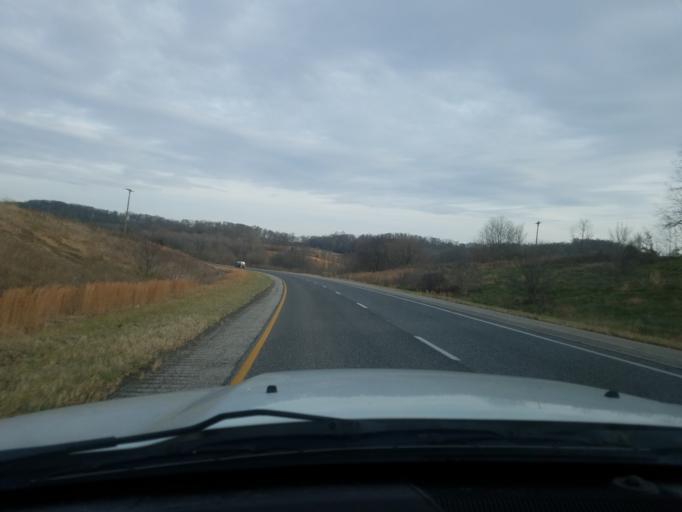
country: US
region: Indiana
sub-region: Dubois County
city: Ferdinand
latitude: 38.2058
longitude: -86.7885
